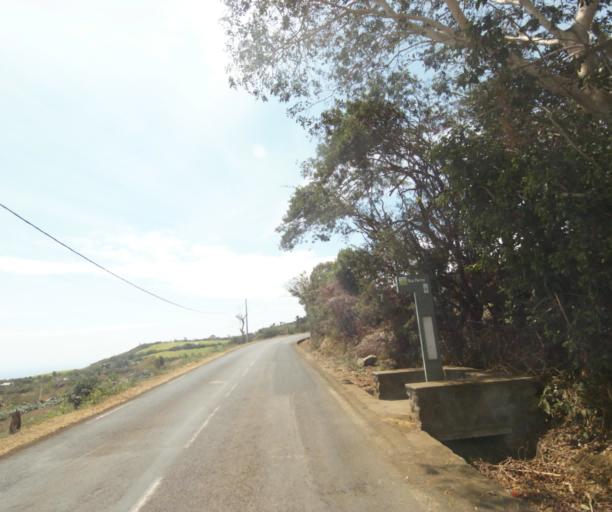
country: RE
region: Reunion
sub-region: Reunion
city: Trois-Bassins
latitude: -21.0969
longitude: 55.2706
